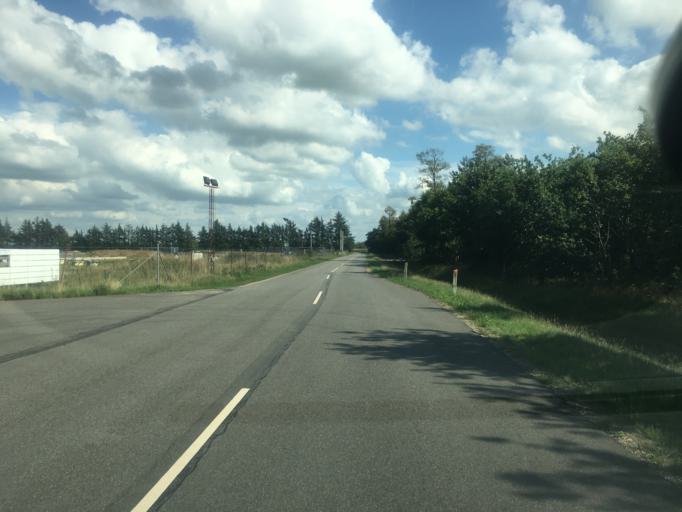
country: DE
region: Schleswig-Holstein
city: Ellhoft
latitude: 54.9667
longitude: 8.9735
